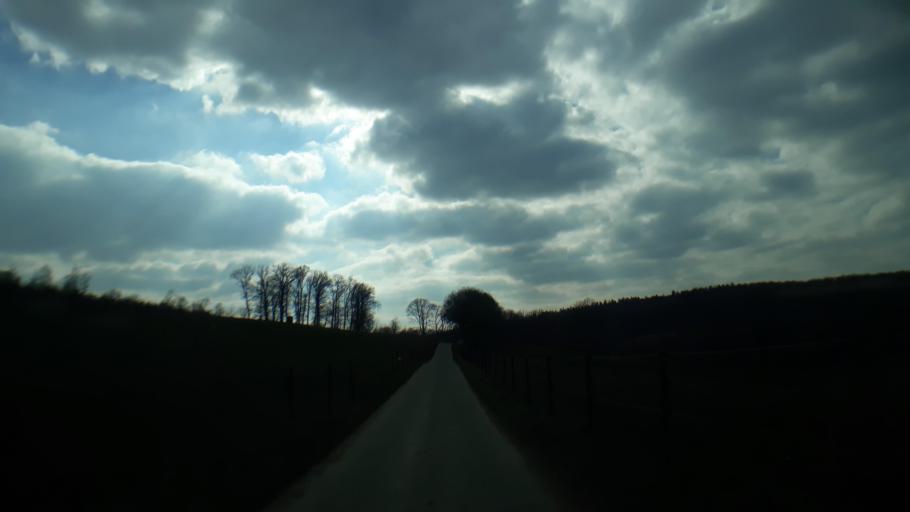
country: DE
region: Rheinland-Pfalz
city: Kirchsahr
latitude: 50.5893
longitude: 6.8901
